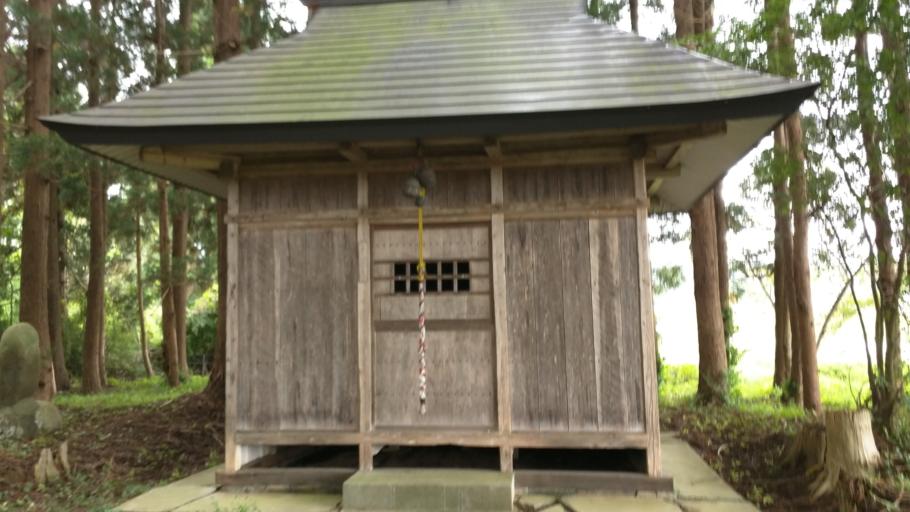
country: JP
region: Fukushima
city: Kitakata
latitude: 37.4938
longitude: 139.8301
